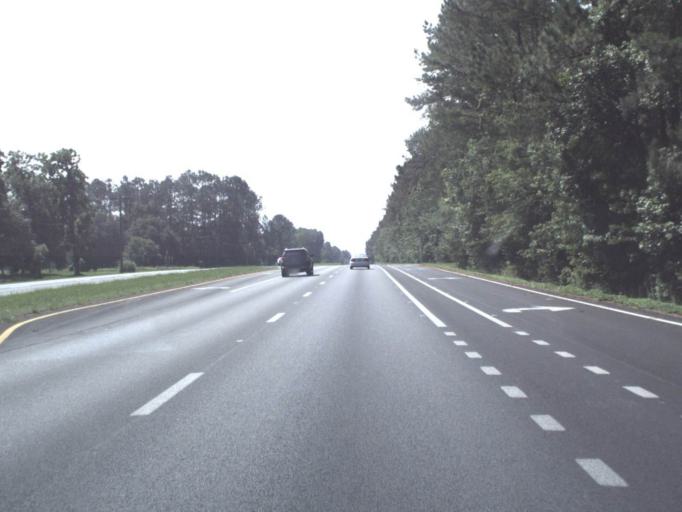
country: US
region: Florida
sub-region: Nassau County
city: Nassau Village-Ratliff
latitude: 30.5396
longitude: -81.8126
